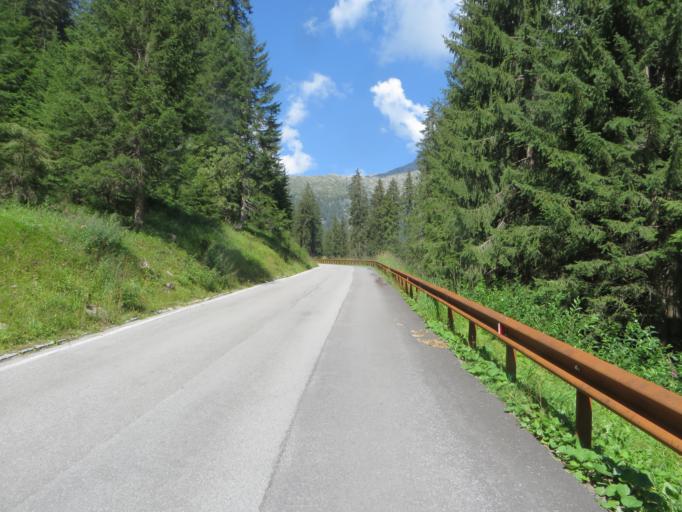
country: IT
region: Trentino-Alto Adige
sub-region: Provincia di Trento
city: Mezzana
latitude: 46.2351
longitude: 10.8152
